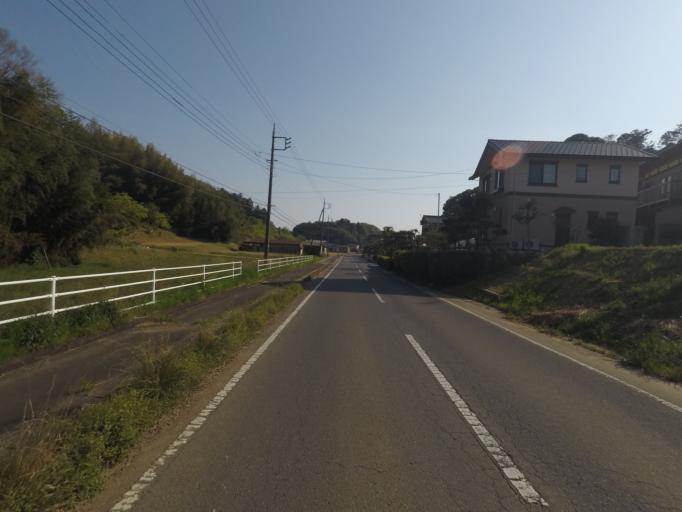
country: JP
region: Ibaraki
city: Inashiki
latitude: 36.0642
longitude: 140.4383
